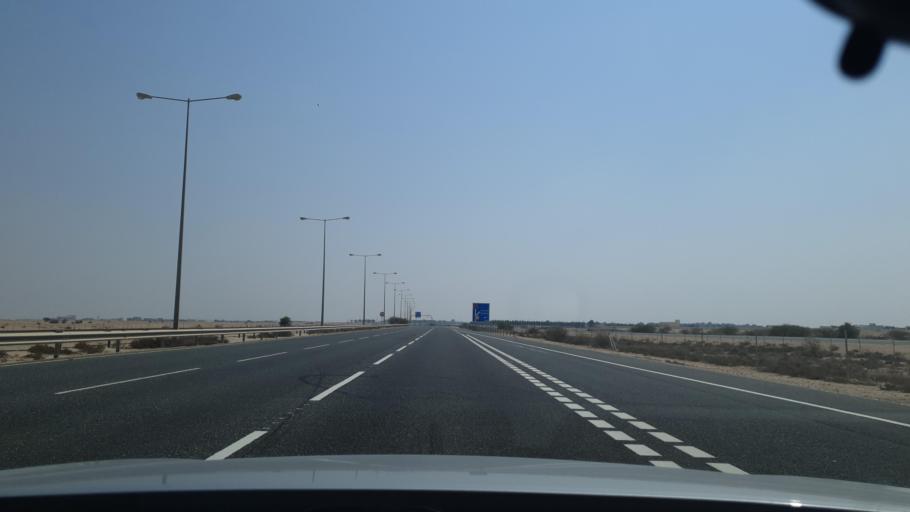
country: QA
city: Al Ghuwayriyah
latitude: 25.7966
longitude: 51.3859
